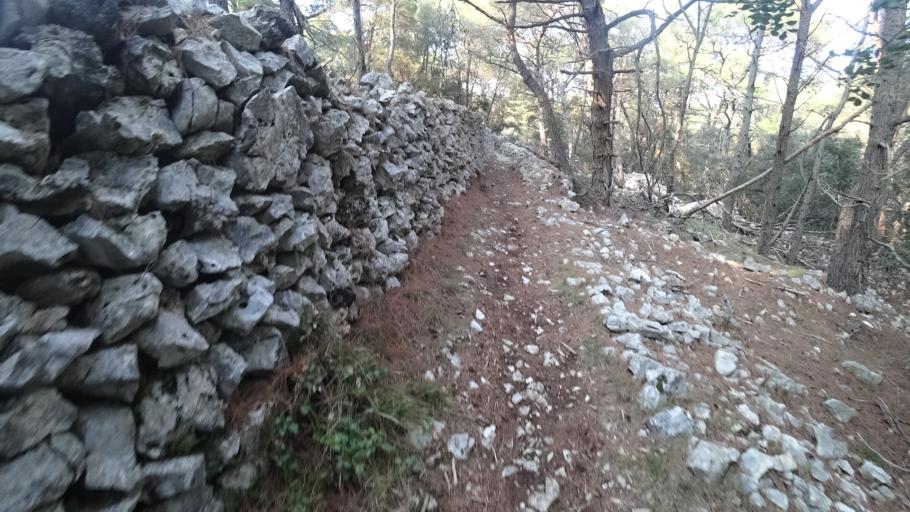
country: HR
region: Primorsko-Goranska
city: Mali Losinj
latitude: 44.5176
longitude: 14.4768
